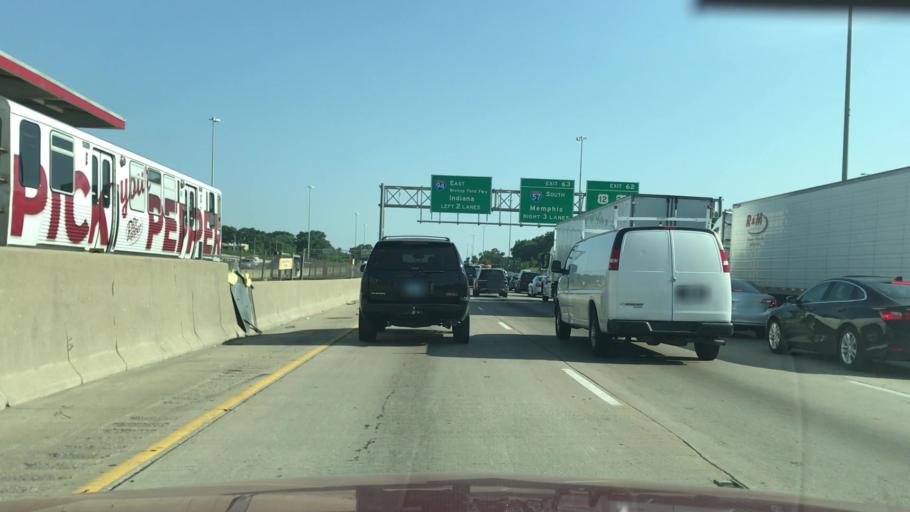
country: US
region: Illinois
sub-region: Cook County
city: Evergreen Park
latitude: 41.7348
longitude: -87.6249
